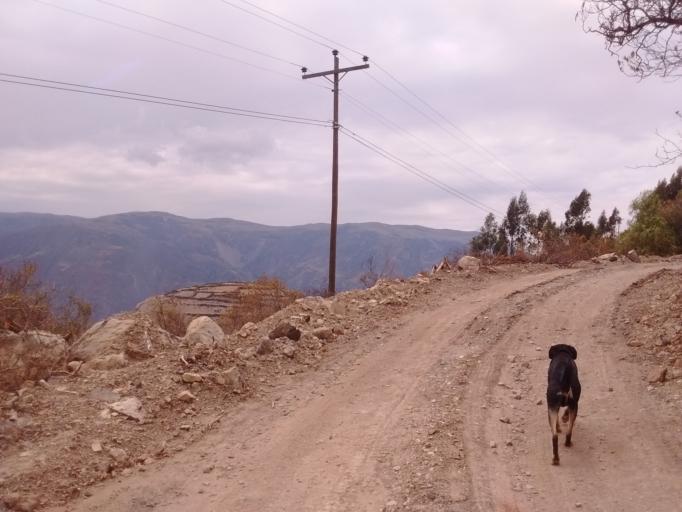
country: PE
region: Ayacucho
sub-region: Provincia de Victor Fajardo
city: Canaria
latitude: -13.8797
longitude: -73.9367
